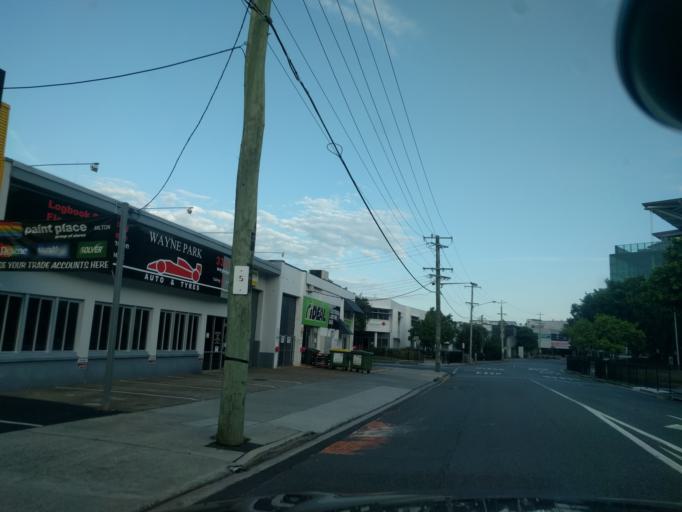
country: AU
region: Queensland
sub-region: Brisbane
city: Milton
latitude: -27.4670
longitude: 153.0088
